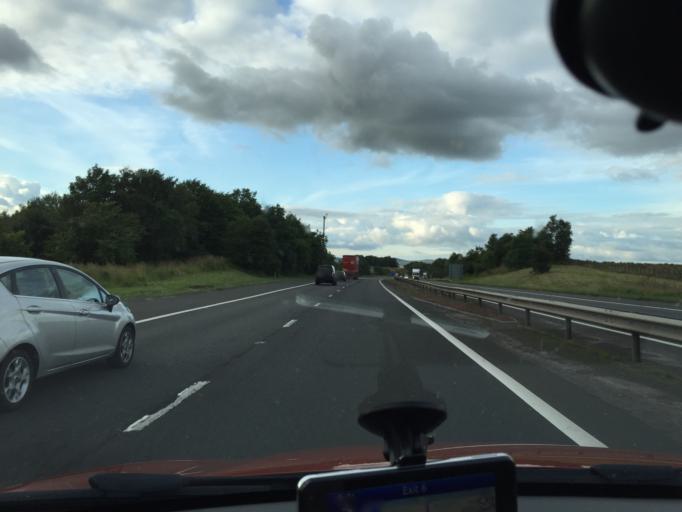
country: GB
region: Scotland
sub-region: North Lanarkshire
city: Glenboig
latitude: 55.8995
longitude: -4.0679
